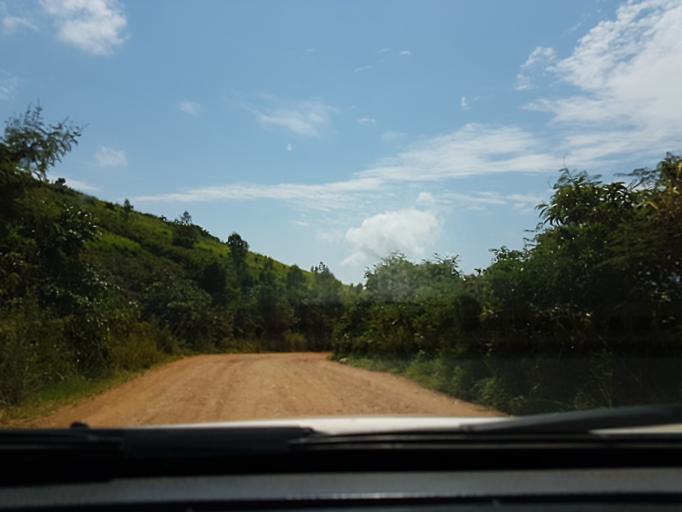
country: RW
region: Western Province
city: Cyangugu
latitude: -2.7019
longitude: 28.9202
